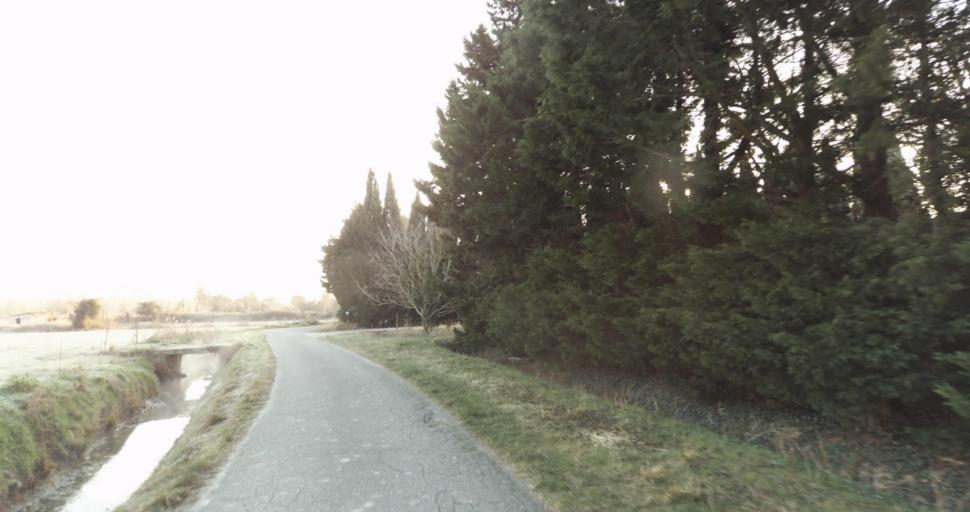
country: FR
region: Provence-Alpes-Cote d'Azur
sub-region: Departement des Bouches-du-Rhone
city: Rognonas
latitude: 43.8994
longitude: 4.7809
